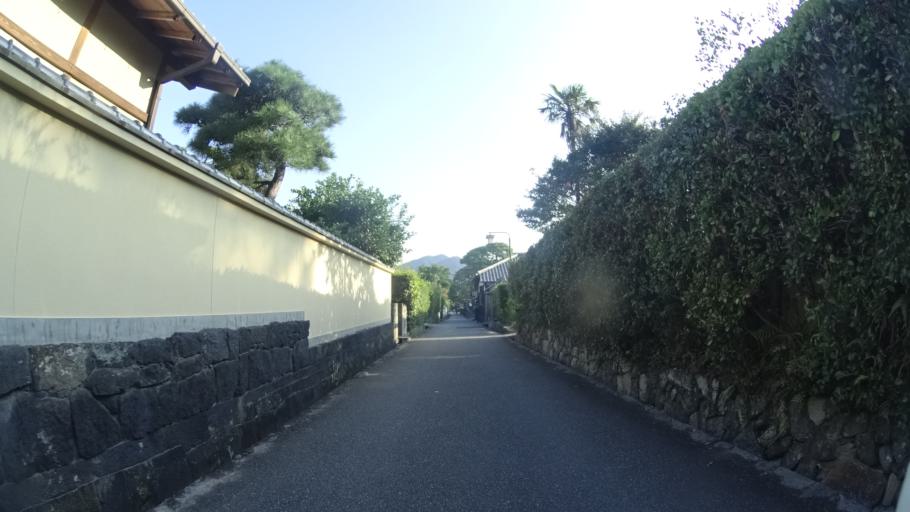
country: JP
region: Yamaguchi
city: Hagi
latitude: 34.4126
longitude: 131.3950
